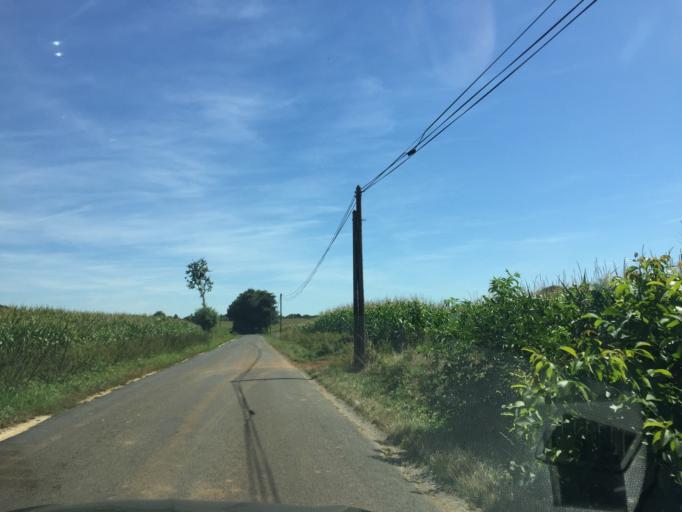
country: FR
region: Poitou-Charentes
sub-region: Departement de la Vienne
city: La Villedieu-du-Clain
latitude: 46.4396
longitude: 0.3225
